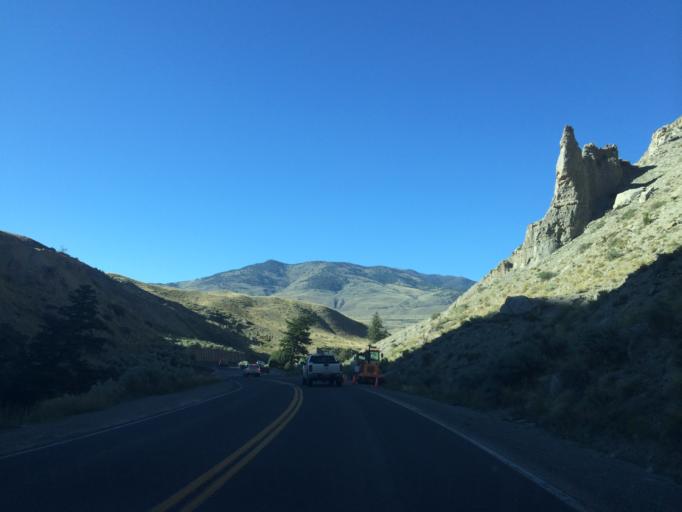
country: US
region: Montana
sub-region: Gallatin County
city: West Yellowstone
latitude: 45.0102
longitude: -110.6938
